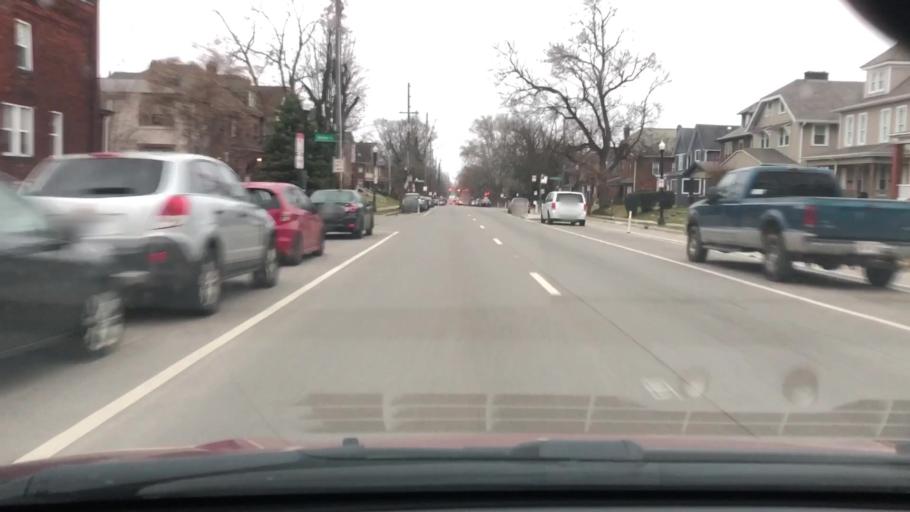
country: US
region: Ohio
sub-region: Franklin County
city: Columbus
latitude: 40.0086
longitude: -83.0005
